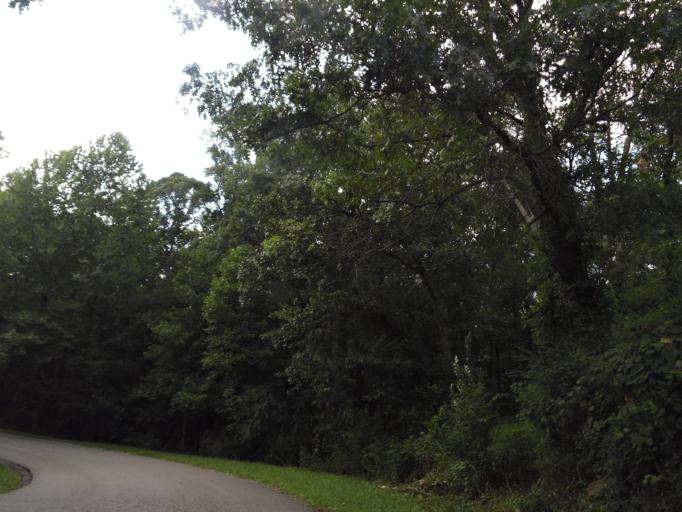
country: US
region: Tennessee
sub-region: Roane County
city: Rockwood
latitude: 35.8903
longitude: -84.7977
